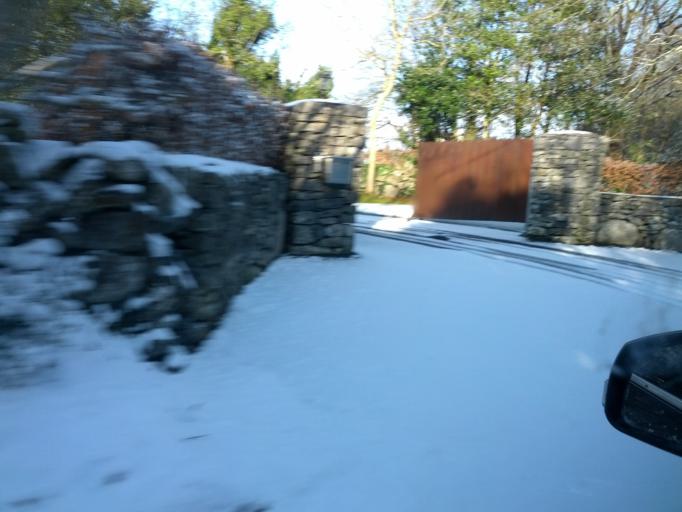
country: IE
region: Connaught
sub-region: County Galway
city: Gort
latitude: 53.1854
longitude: -8.8269
